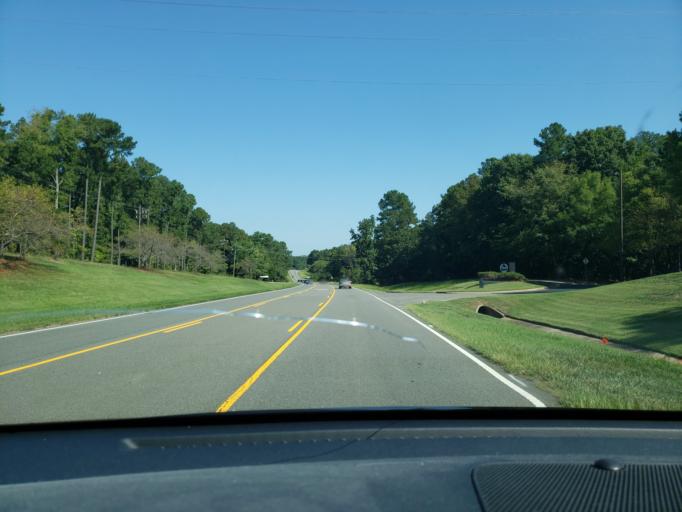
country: US
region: North Carolina
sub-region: Durham County
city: Durham
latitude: 35.9076
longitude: -78.8780
